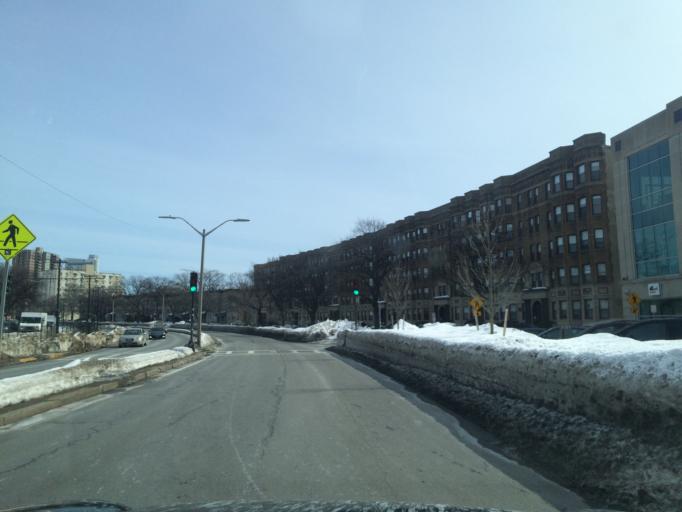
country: US
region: Massachusetts
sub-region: Norfolk County
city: Brookline
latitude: 42.3504
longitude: -71.1285
